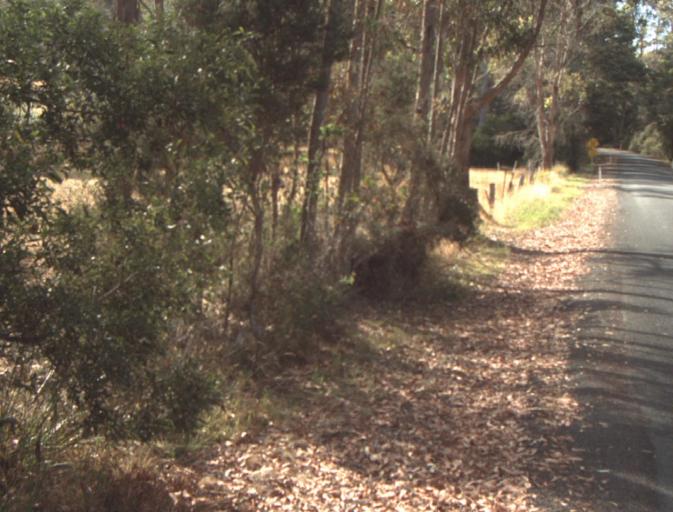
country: AU
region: Tasmania
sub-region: Launceston
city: Mayfield
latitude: -41.2686
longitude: 147.1613
